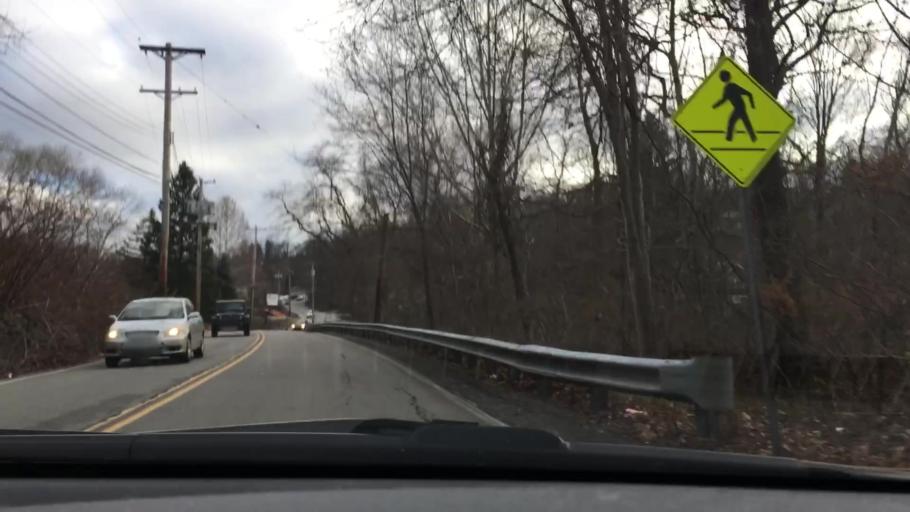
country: US
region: Pennsylvania
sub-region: Allegheny County
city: North Versailles
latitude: 40.3726
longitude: -79.8055
